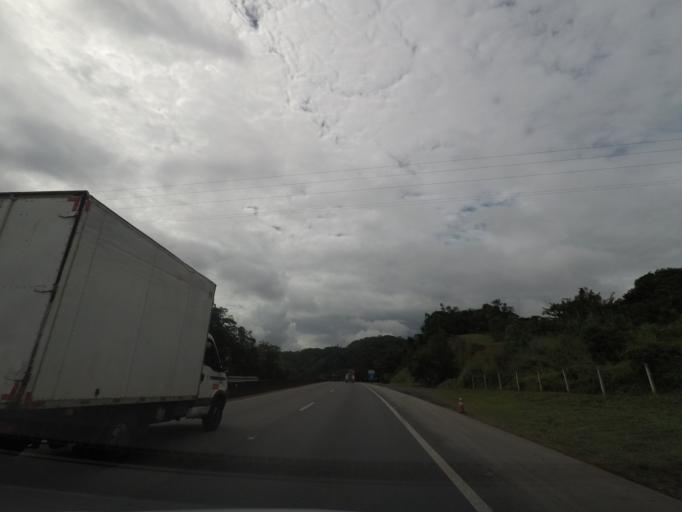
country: BR
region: Sao Paulo
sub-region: Miracatu
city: Miracatu
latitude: -24.2416
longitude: -47.3632
